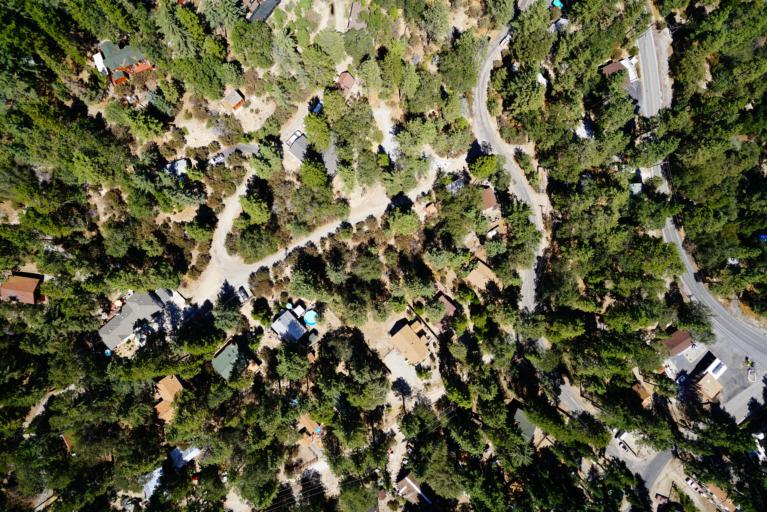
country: US
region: California
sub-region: Riverside County
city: Idyllwild-Pine Cove
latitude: 33.7597
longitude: -116.7401
